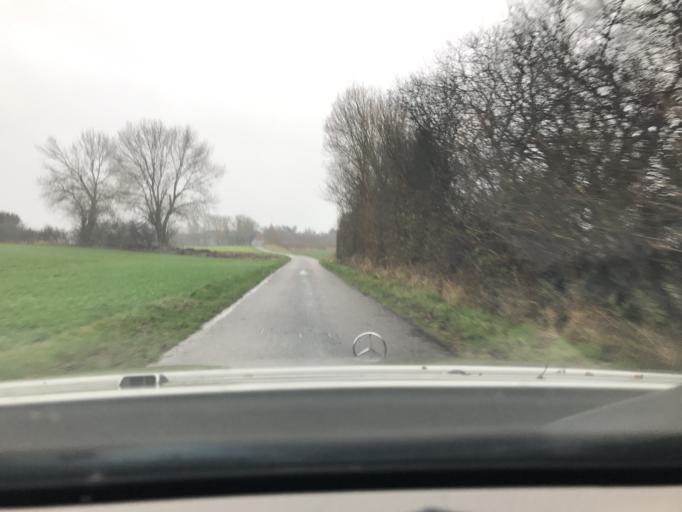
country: DE
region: Schleswig-Holstein
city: Pommerby
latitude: 54.8807
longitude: 10.0642
